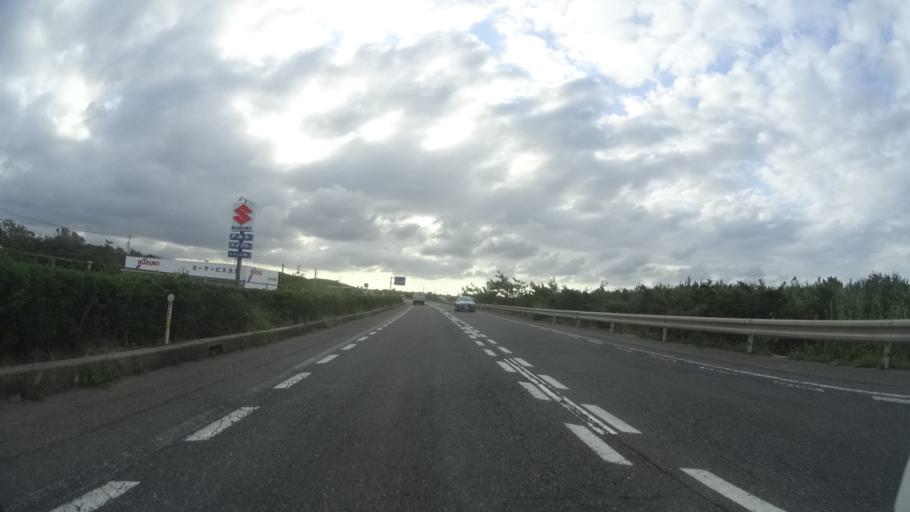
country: JP
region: Tottori
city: Kurayoshi
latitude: 35.5017
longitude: 133.7284
